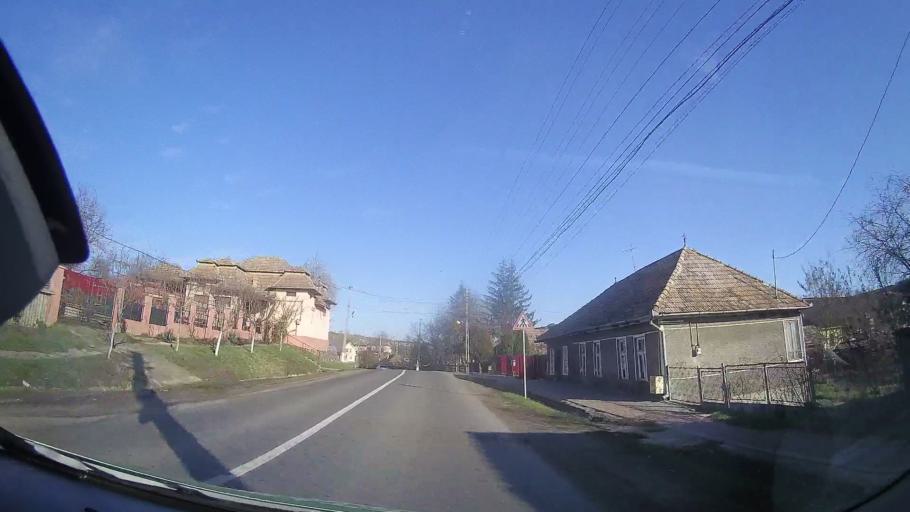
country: RO
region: Mures
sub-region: Comuna Zau De Campie
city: Zau de Campie
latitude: 46.6182
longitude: 24.1278
